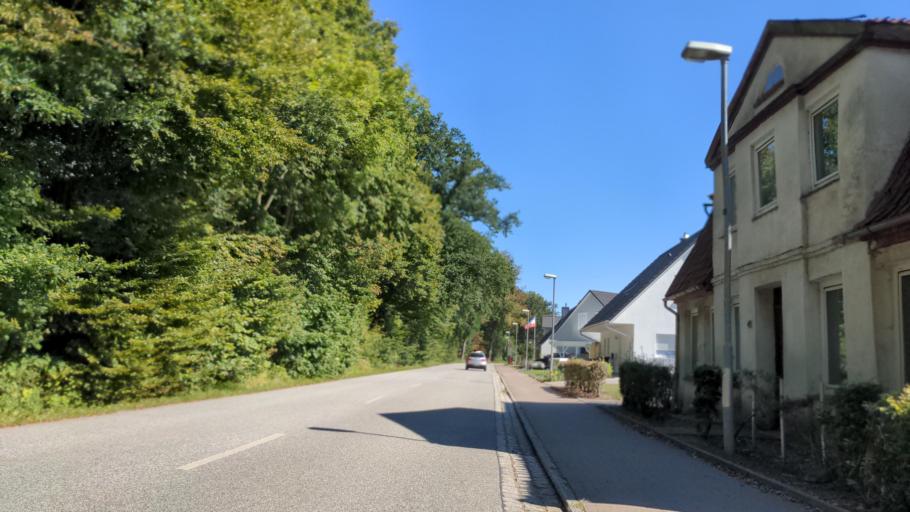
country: DE
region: Schleswig-Holstein
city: Hamberge
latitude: 53.8299
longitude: 10.6059
